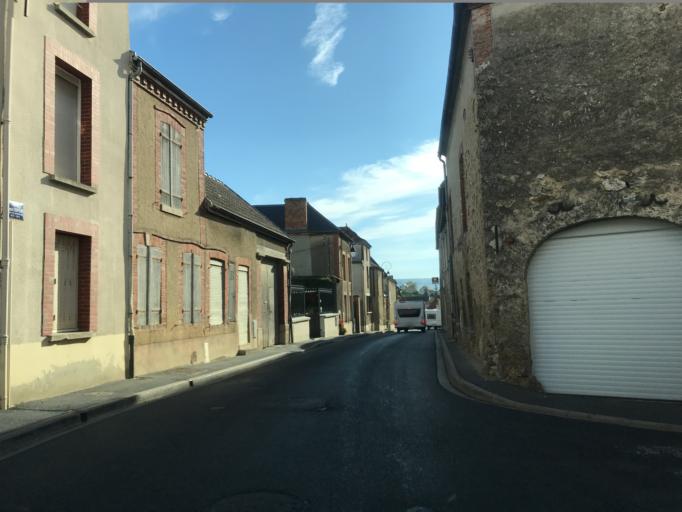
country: FR
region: Champagne-Ardenne
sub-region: Departement de la Marne
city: Mardeuil
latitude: 49.0730
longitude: 3.9274
